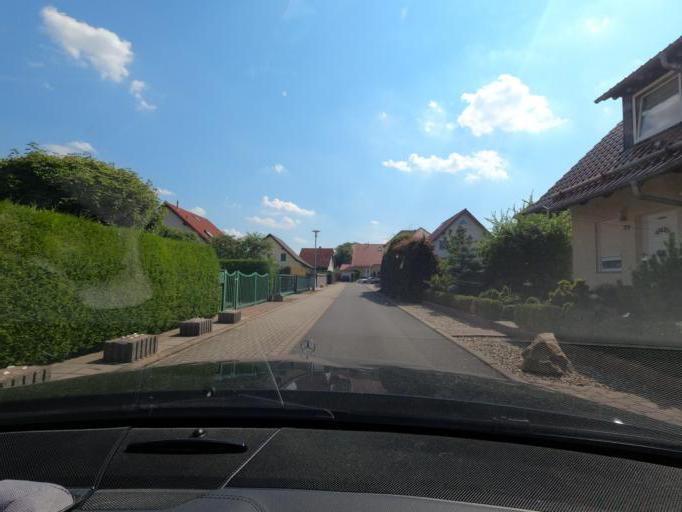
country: DE
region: Thuringia
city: Nordhausen
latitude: 51.5143
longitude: 10.7637
